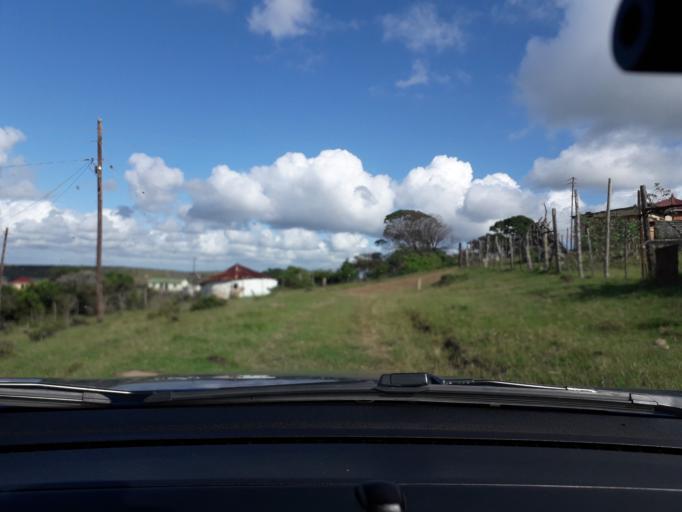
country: ZA
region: Eastern Cape
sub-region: Buffalo City Metropolitan Municipality
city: Bhisho
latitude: -33.1130
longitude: 27.4304
